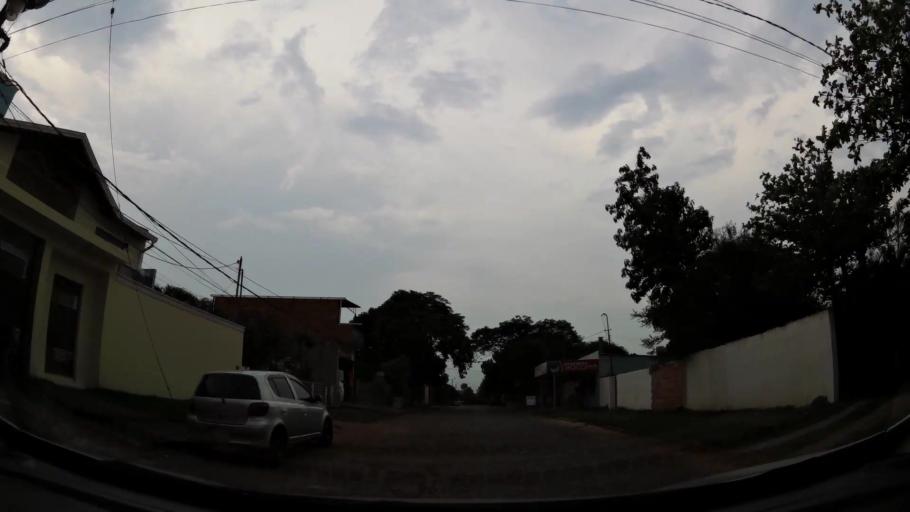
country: PY
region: Alto Parana
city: Presidente Franco
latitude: -25.5389
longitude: -54.6039
